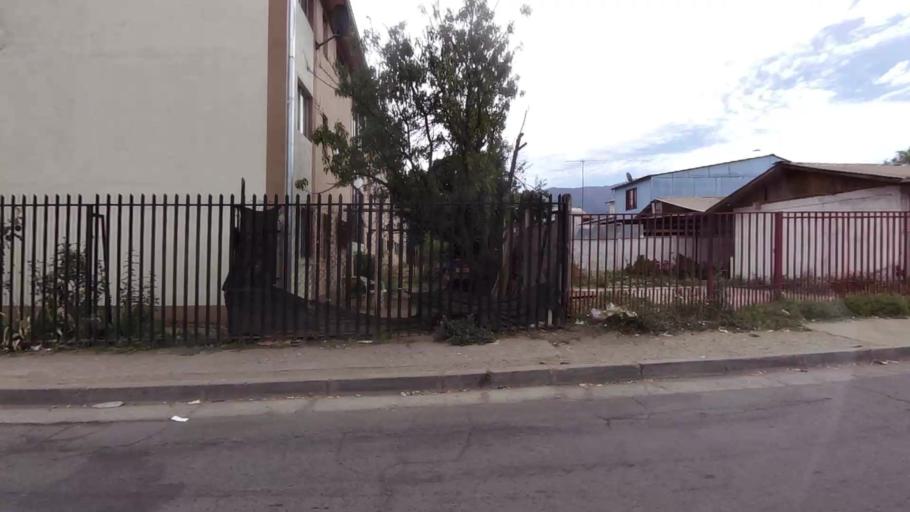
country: CL
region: O'Higgins
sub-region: Provincia de Cachapoal
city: Graneros
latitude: -34.0676
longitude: -70.7233
